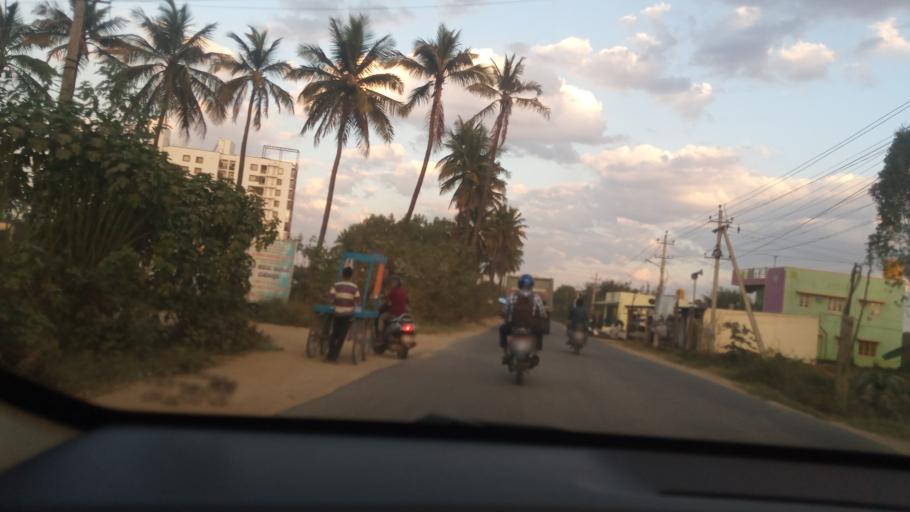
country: IN
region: Karnataka
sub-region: Bangalore Rural
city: Hoskote
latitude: 12.9794
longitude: 77.7930
